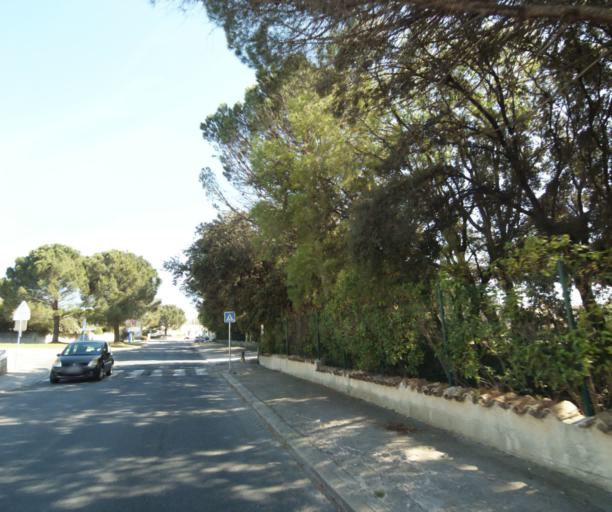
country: FR
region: Languedoc-Roussillon
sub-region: Departement de l'Herault
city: Le Cres
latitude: 43.6413
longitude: 3.9350
